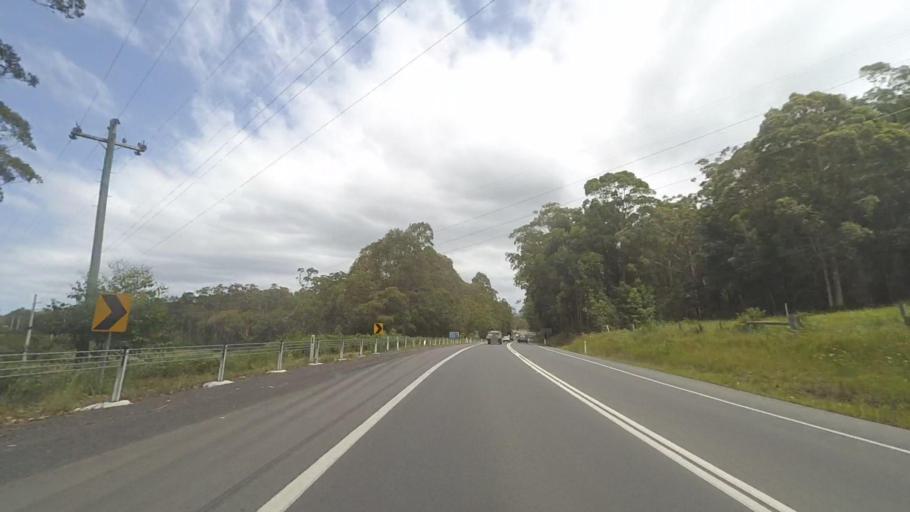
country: AU
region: New South Wales
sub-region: Shoalhaven Shire
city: Falls Creek
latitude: -35.0852
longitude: 150.5396
